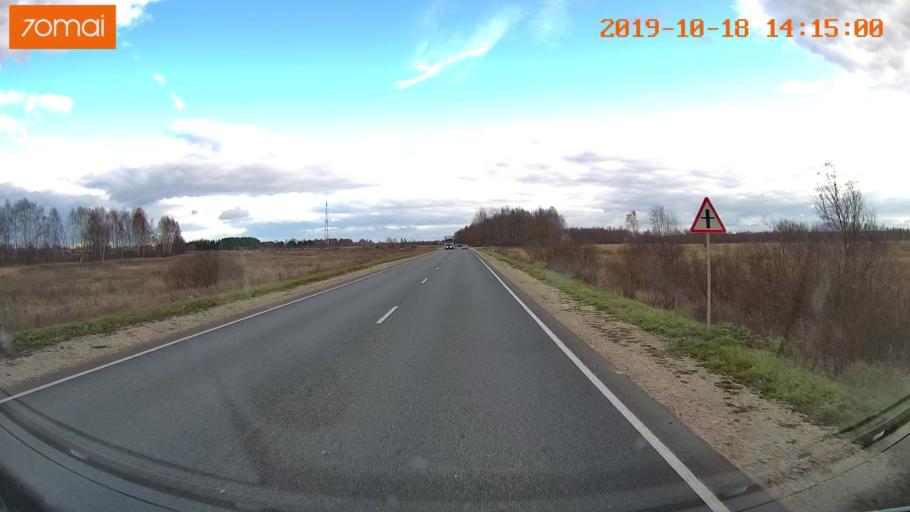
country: RU
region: Rjazan
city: Spas-Klepiki
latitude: 55.1471
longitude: 40.3080
